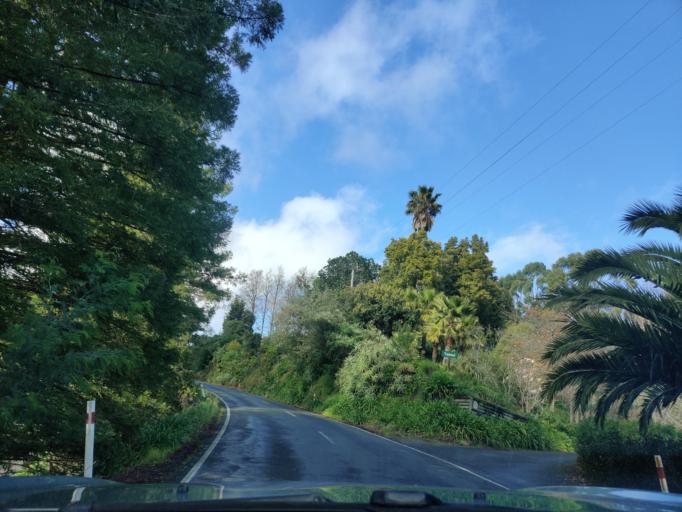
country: NZ
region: Hawke's Bay
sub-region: Hastings District
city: Hastings
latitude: -39.6816
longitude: 176.8972
